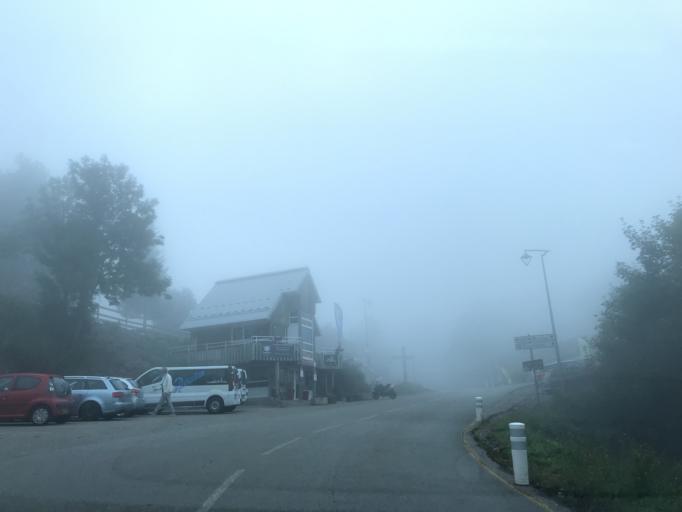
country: FR
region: Rhone-Alpes
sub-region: Departement de la Haute-Savoie
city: Doussard
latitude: 45.8091
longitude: 6.2444
